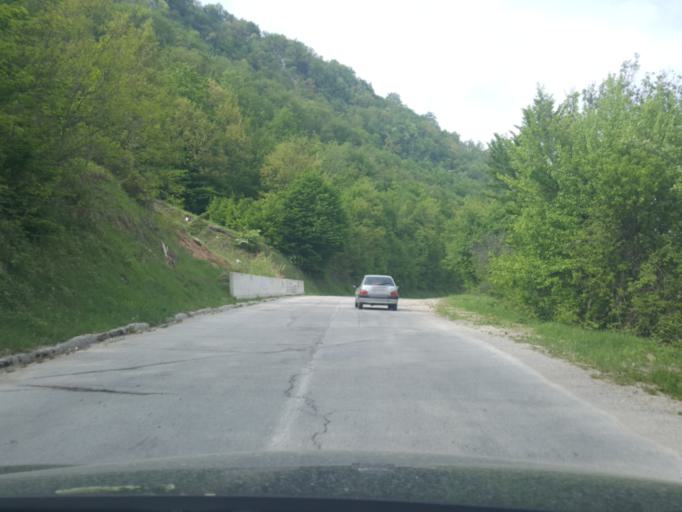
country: RS
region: Central Serbia
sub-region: Zlatiborski Okrug
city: Bajina Basta
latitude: 44.0936
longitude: 19.6626
